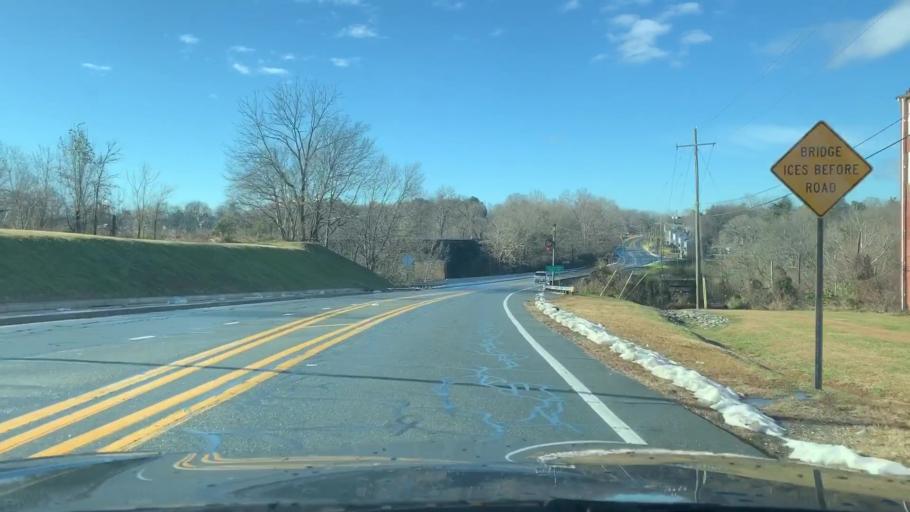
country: US
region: North Carolina
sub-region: Alamance County
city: Haw River
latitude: 36.0894
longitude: -79.3669
